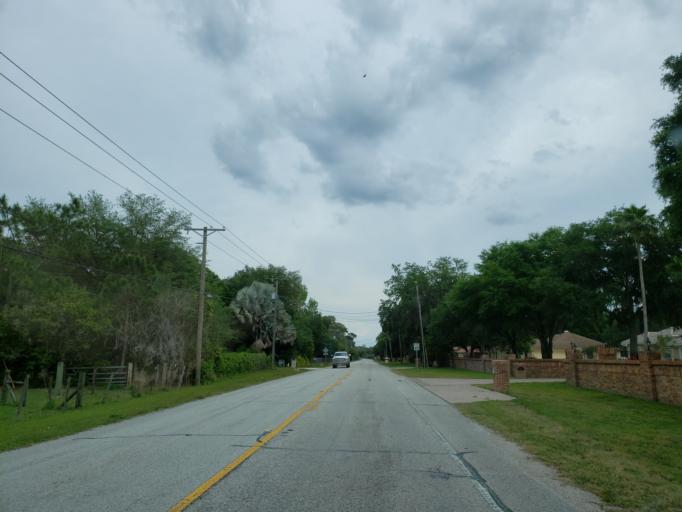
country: US
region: Florida
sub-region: Hillsborough County
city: Keystone
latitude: 28.1403
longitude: -82.6364
